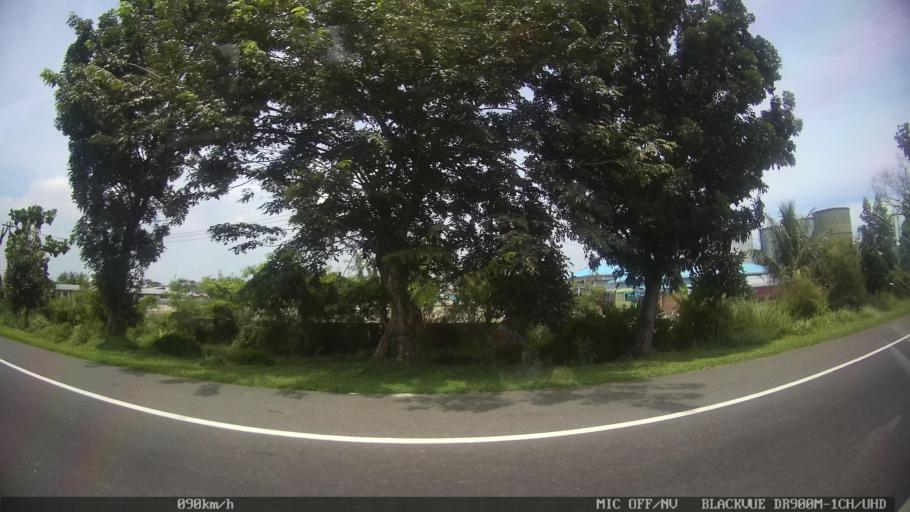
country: ID
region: North Sumatra
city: Labuhan Deli
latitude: 3.7240
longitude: 98.6822
